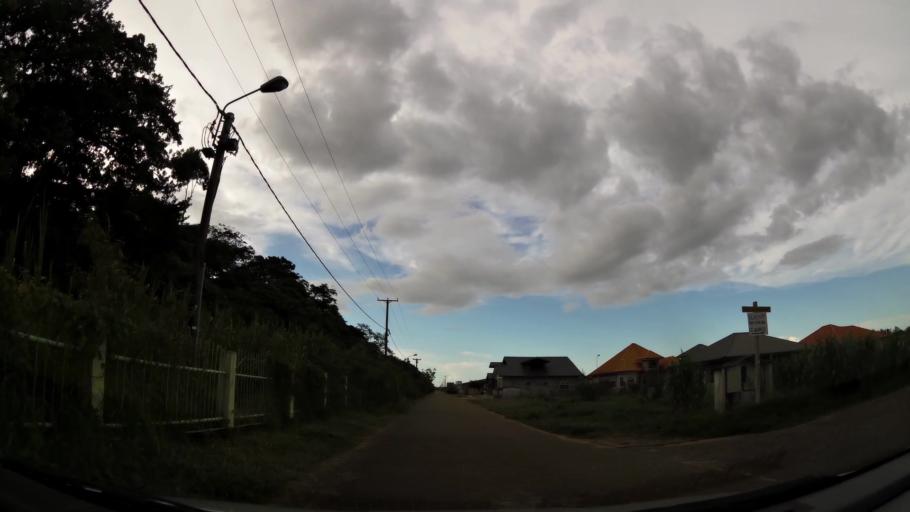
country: SR
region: Paramaribo
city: Paramaribo
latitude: 5.8648
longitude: -55.1768
